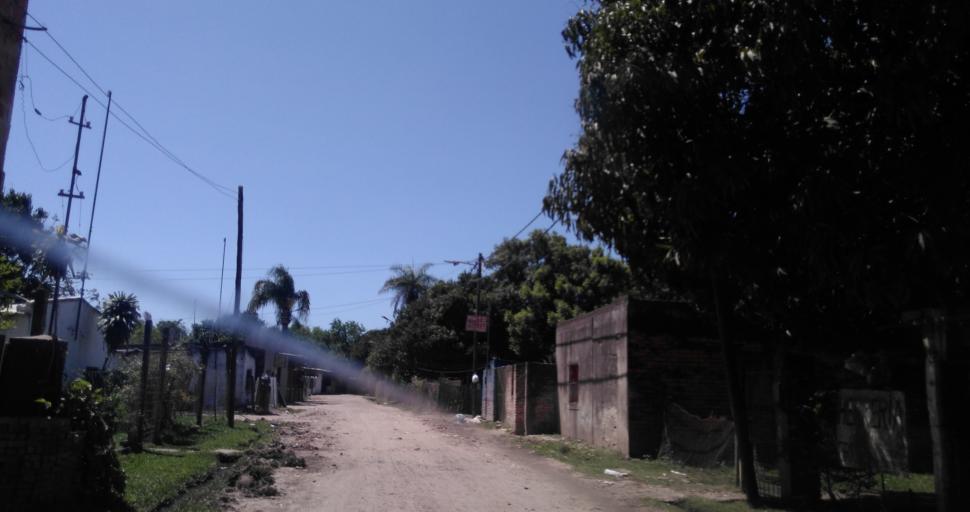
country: AR
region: Chaco
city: Resistencia
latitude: -27.4247
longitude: -58.9809
